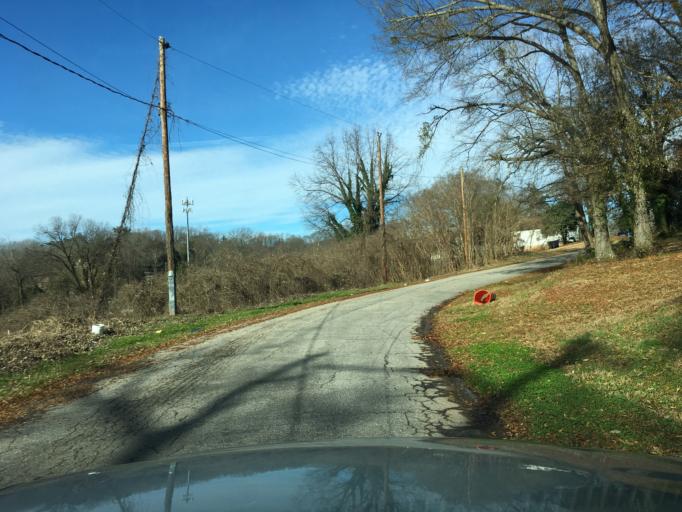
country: US
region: South Carolina
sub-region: Greenville County
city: Greenville
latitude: 34.8557
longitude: -82.3837
